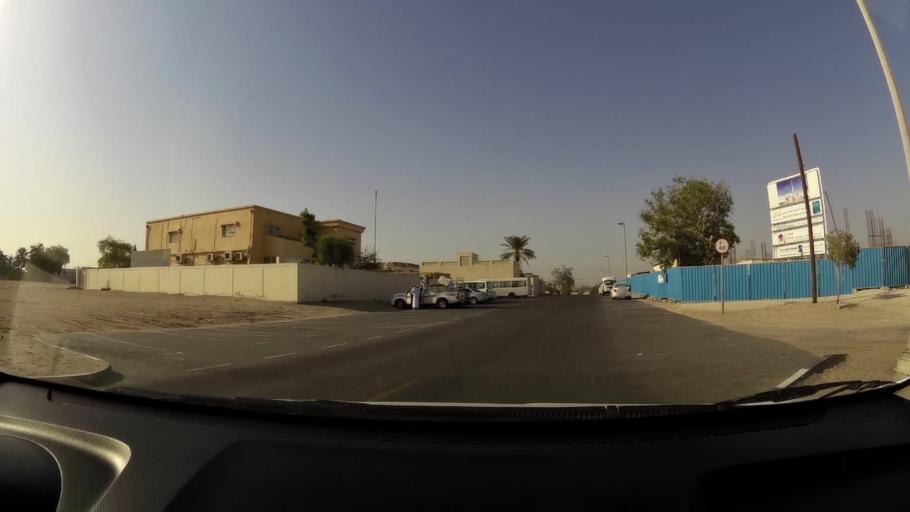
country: AE
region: Ash Shariqah
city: Sharjah
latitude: 25.2683
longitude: 55.3890
